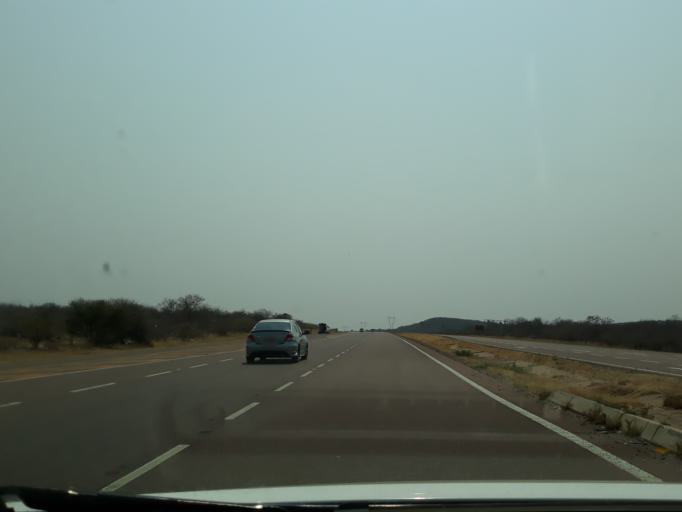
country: BW
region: Kgatleng
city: Bokaa
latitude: -24.4022
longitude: 26.0560
